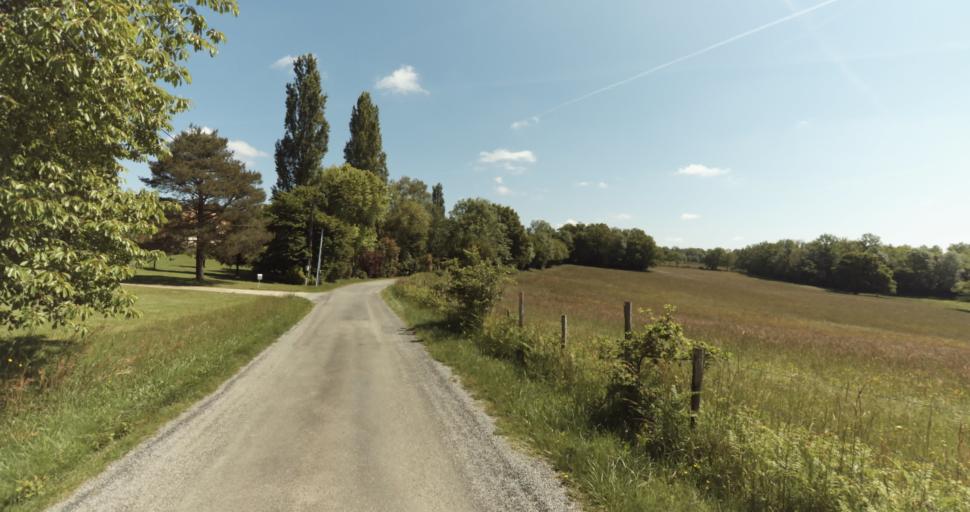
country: FR
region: Limousin
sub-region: Departement de la Haute-Vienne
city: Le Vigen
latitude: 45.7603
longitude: 1.3089
